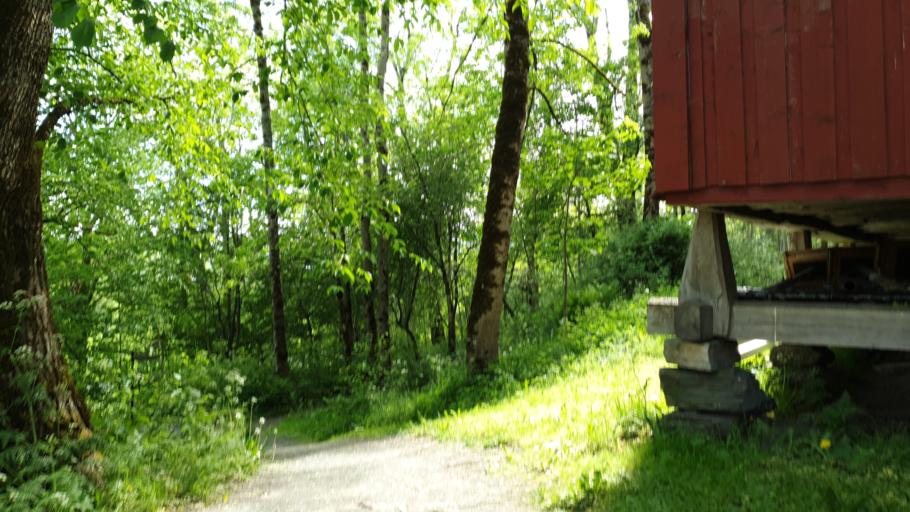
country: NO
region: Sor-Trondelag
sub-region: Rissa
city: Rissa
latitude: 63.5643
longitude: 9.9209
